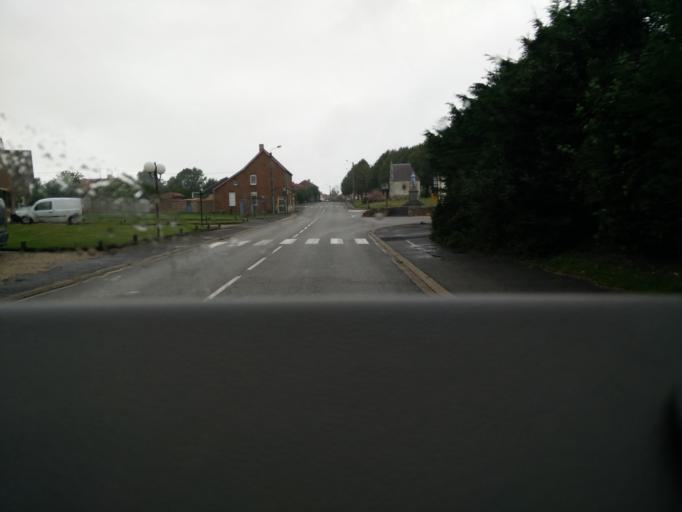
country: FR
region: Nord-Pas-de-Calais
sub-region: Departement du Pas-de-Calais
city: Bouvigny-Boyeffles
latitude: 50.4073
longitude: 2.6353
